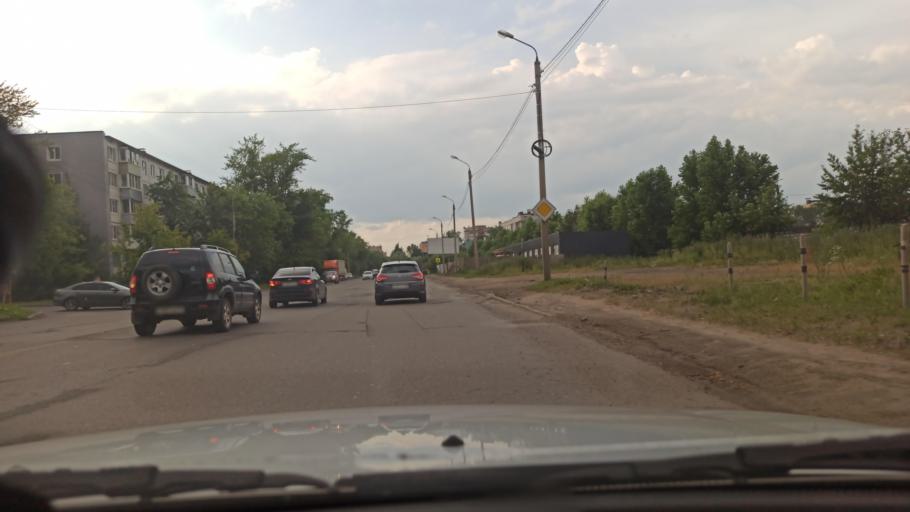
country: RU
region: Vologda
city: Vologda
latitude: 59.2040
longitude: 39.8525
